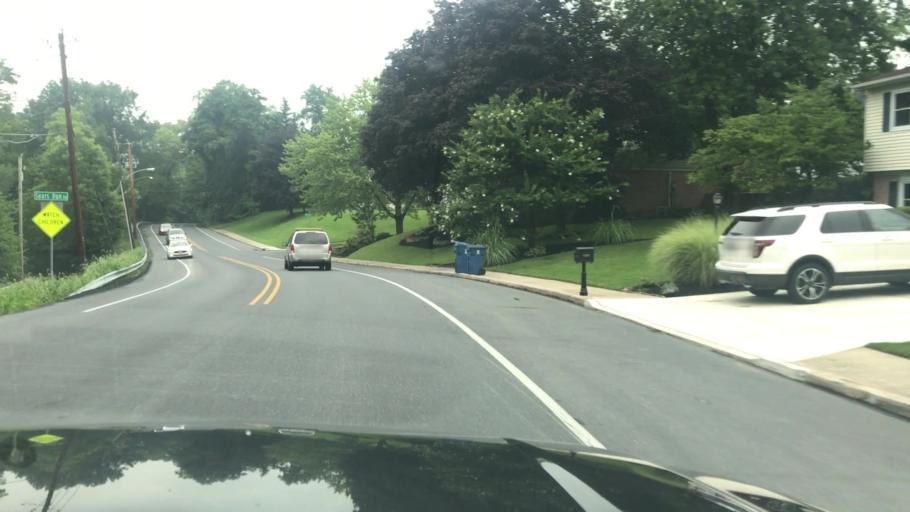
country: US
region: Pennsylvania
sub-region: Cumberland County
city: Shiremanstown
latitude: 40.2571
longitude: -76.9595
